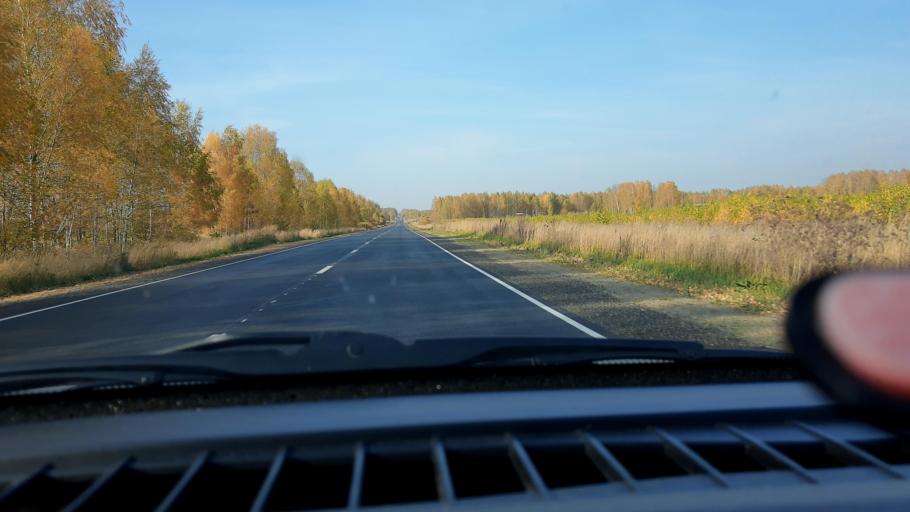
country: RU
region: Nizjnij Novgorod
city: Novaya Balakhna
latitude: 56.5794
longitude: 43.6907
